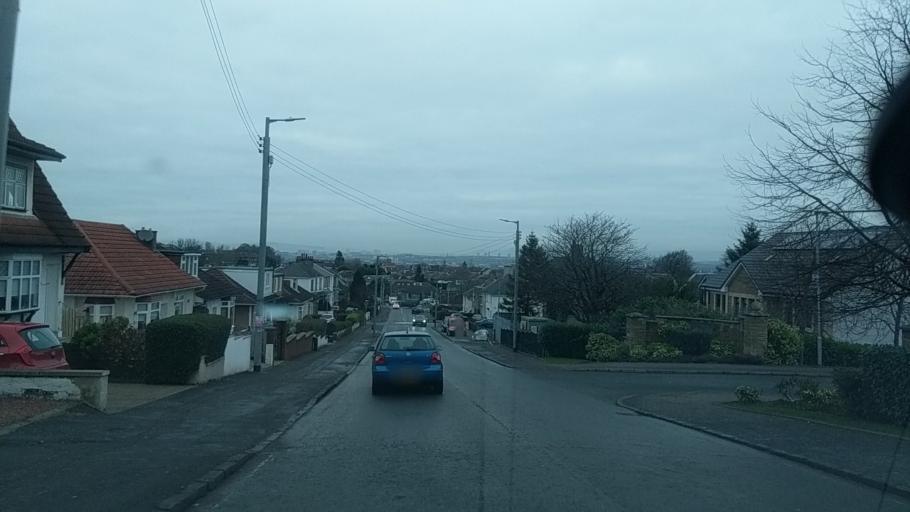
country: GB
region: Scotland
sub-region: South Lanarkshire
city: Rutherglen
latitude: 55.8168
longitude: -4.1891
